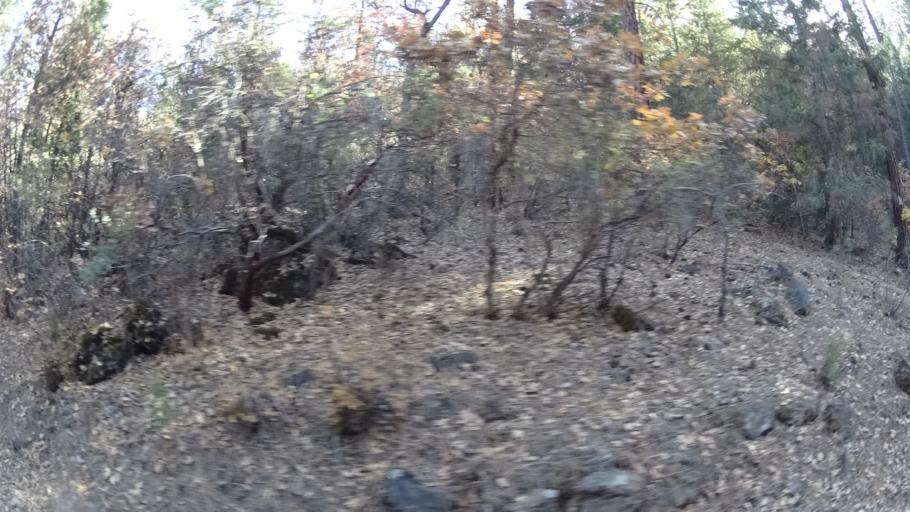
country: US
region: California
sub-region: Siskiyou County
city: Yreka
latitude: 41.8616
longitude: -122.8188
